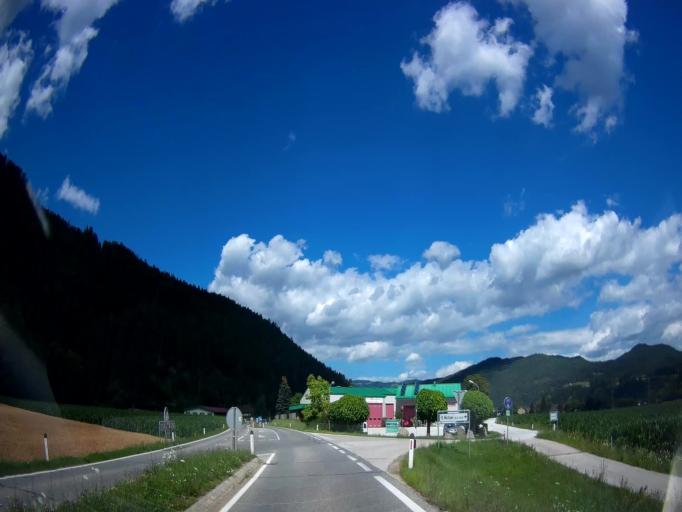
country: AT
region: Carinthia
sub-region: Politischer Bezirk Klagenfurt Land
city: Poggersdorf
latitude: 46.6880
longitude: 14.4799
